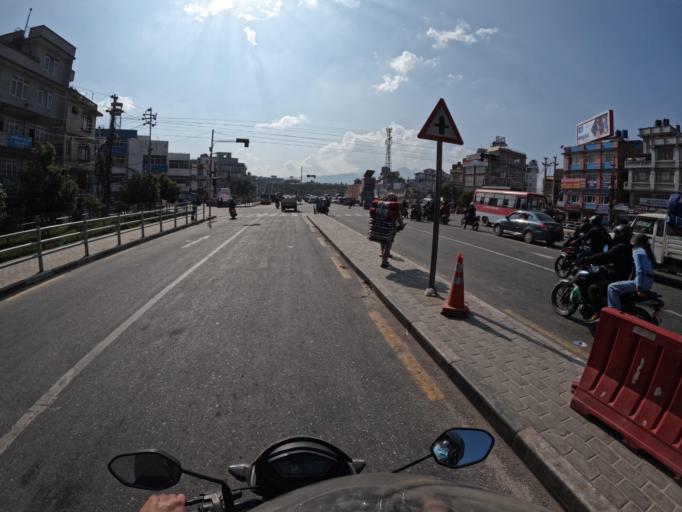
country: NP
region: Central Region
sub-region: Bagmati Zone
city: Patan
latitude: 27.6588
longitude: 85.3252
